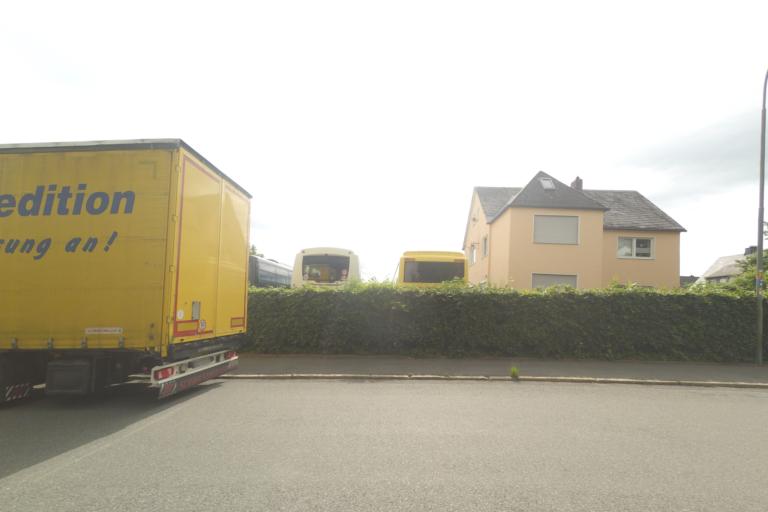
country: DE
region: Bavaria
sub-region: Upper Franconia
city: Munchberg
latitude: 50.1831
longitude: 11.7916
